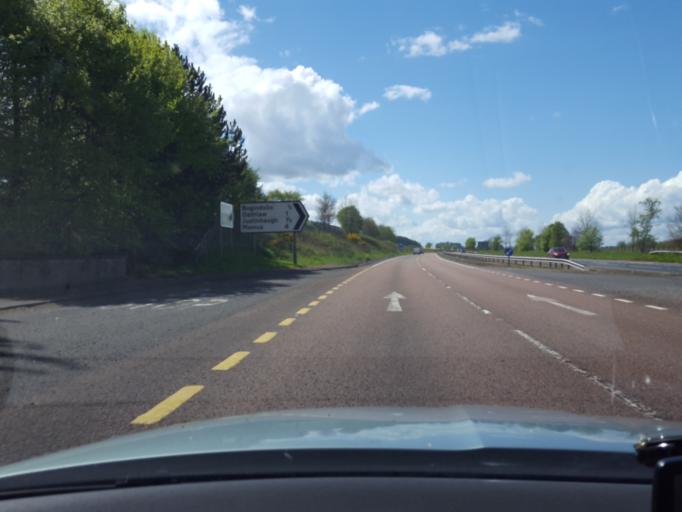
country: GB
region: Scotland
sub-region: Angus
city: Forfar
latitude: 56.6833
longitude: -2.8594
